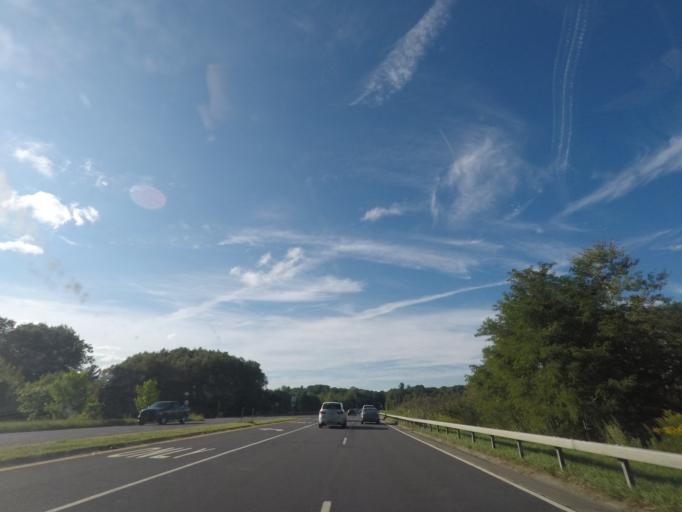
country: US
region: New York
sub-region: Albany County
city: Colonie
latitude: 42.7474
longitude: -73.8175
